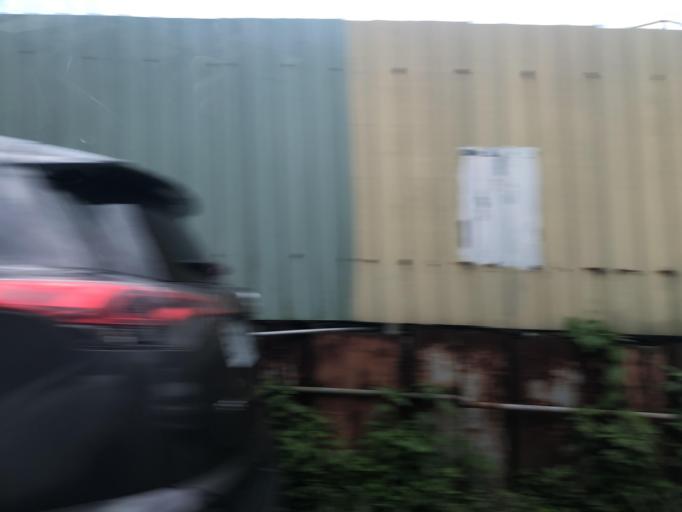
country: TW
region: Taipei
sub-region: Taipei
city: Banqiao
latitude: 24.9193
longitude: 121.4322
